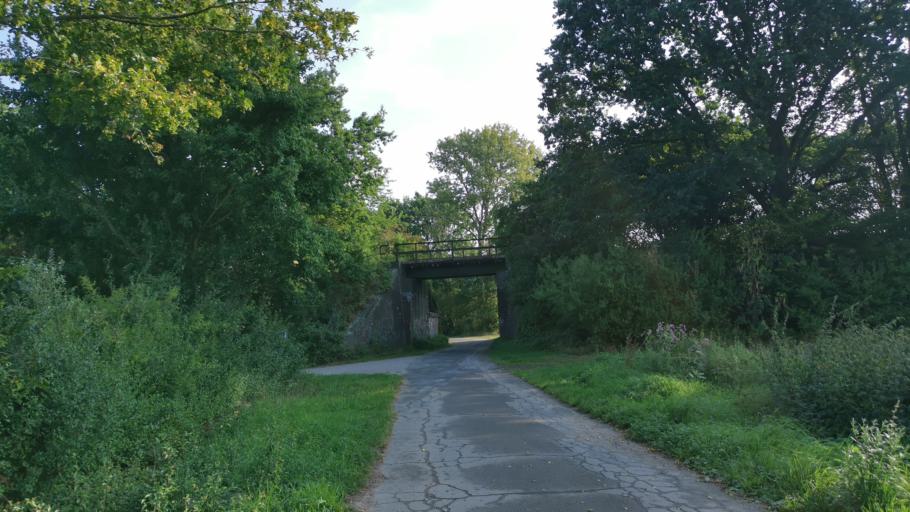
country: DE
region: Schleswig-Holstein
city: Sterley
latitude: 53.6156
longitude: 10.8051
